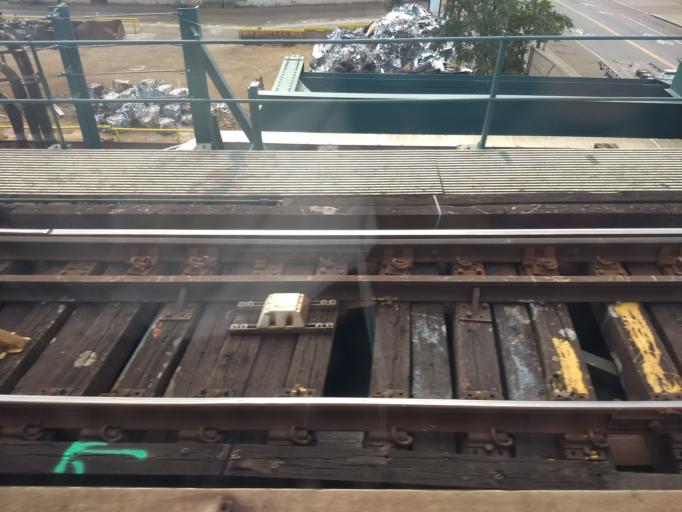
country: US
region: New York
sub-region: Kings County
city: East New York
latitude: 40.6707
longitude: -73.9023
